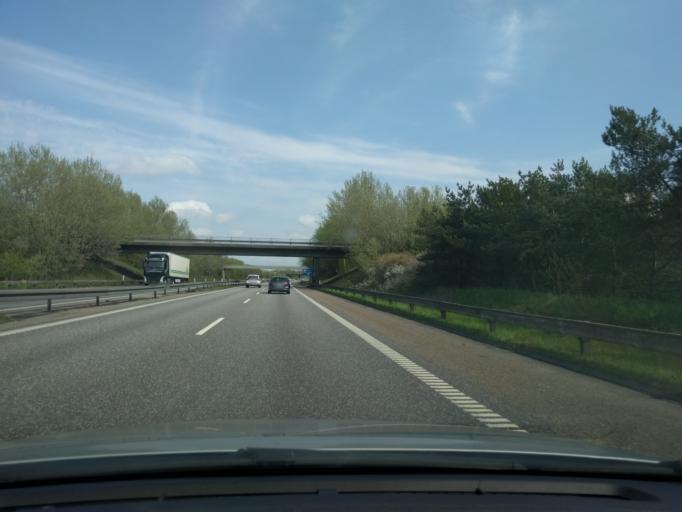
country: DK
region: Zealand
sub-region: Soro Kommune
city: Soro
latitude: 55.4541
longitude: 11.5551
